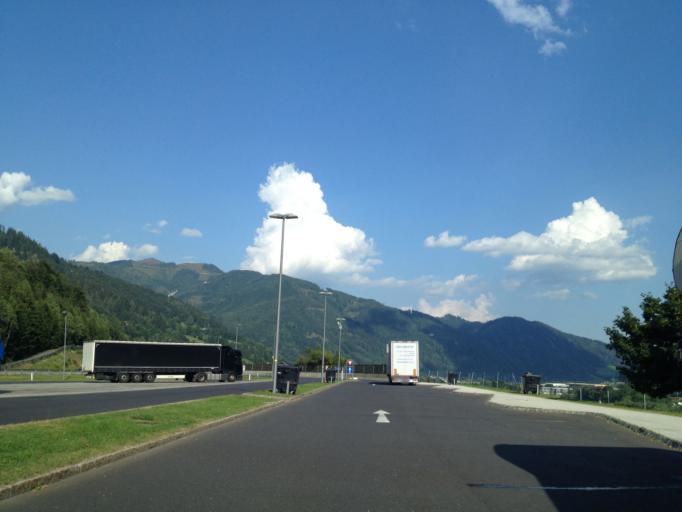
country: AT
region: Styria
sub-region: Politischer Bezirk Leoben
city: Kalwang
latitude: 47.4261
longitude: 14.7233
